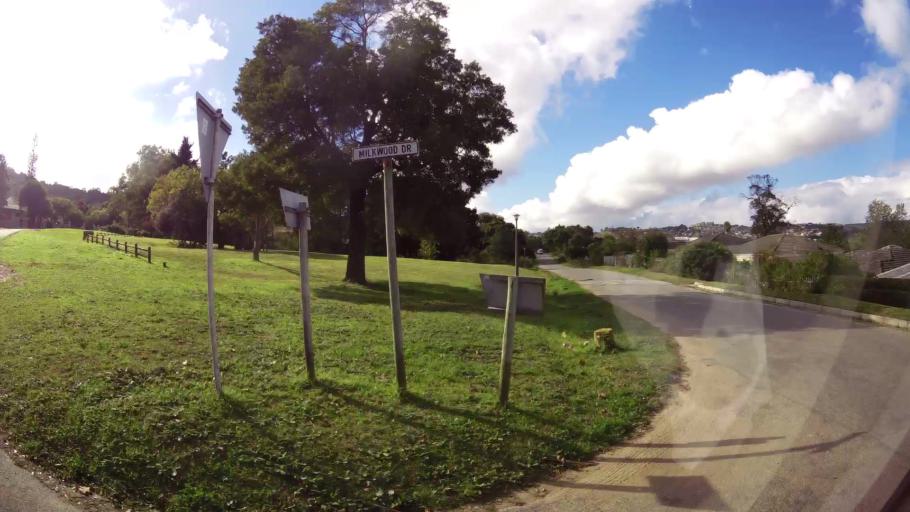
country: ZA
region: Western Cape
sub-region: Eden District Municipality
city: Knysna
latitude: -34.0388
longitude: 23.0715
